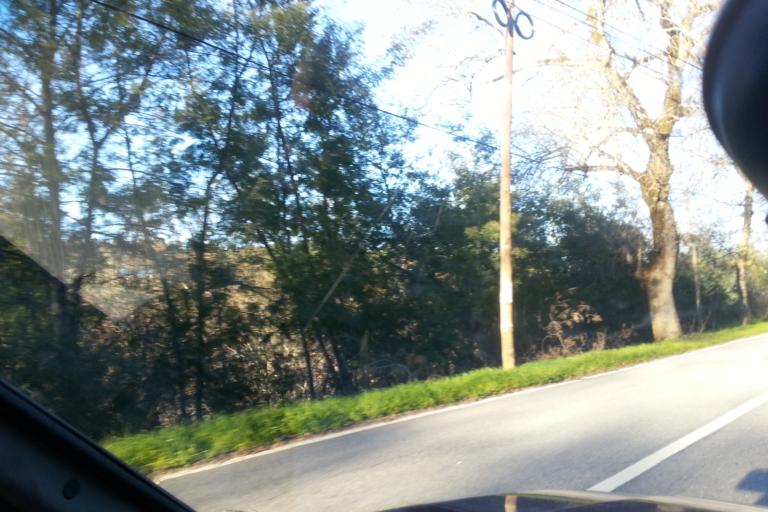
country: PT
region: Guarda
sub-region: Fornos de Algodres
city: Fornos de Algodres
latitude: 40.6153
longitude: -7.5080
